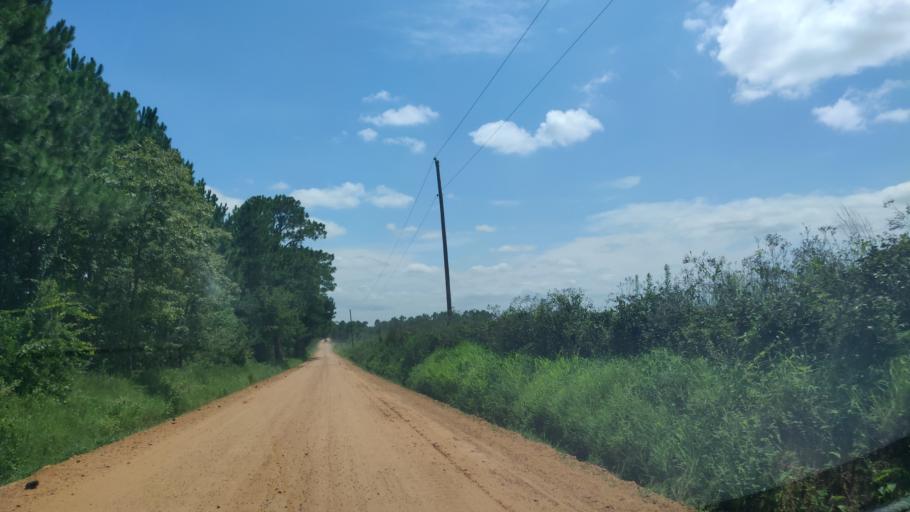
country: US
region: Georgia
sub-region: Tift County
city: Tifton
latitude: 31.4667
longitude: -83.6374
